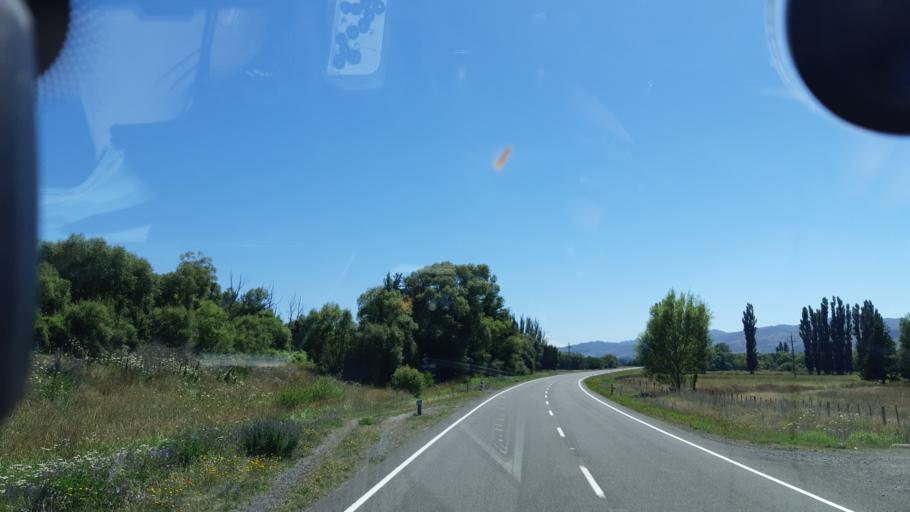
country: NZ
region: Canterbury
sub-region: Kaikoura District
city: Kaikoura
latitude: -42.7304
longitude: 173.2757
